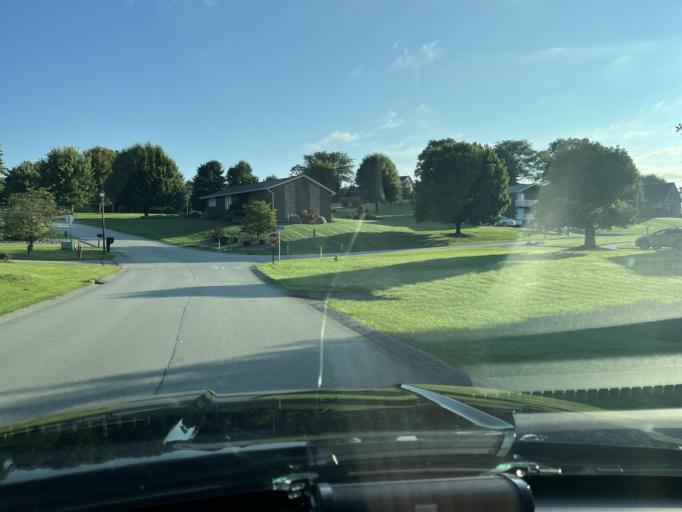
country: US
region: Pennsylvania
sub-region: Fayette County
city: Leith-Hatfield
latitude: 39.8762
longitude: -79.7260
